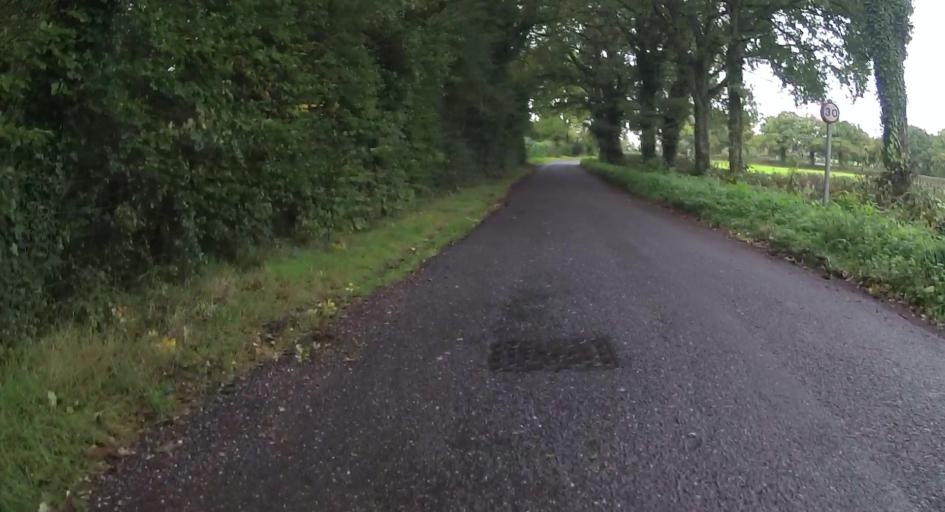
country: GB
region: England
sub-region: Hampshire
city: Tadley
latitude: 51.3231
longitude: -1.1555
